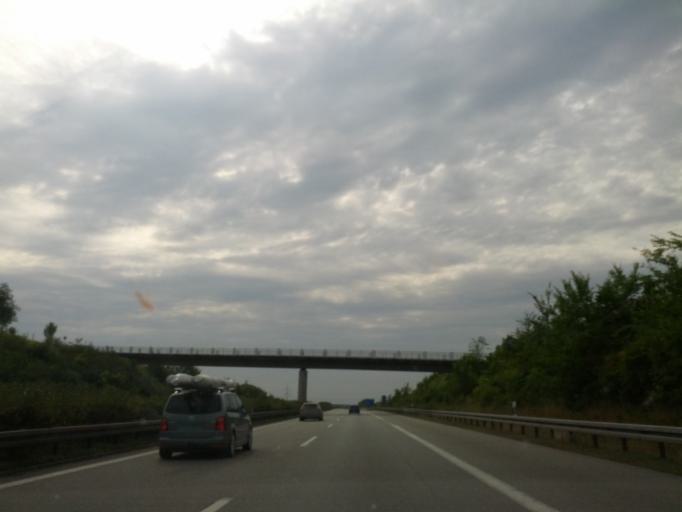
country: DE
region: Mecklenburg-Vorpommern
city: Papendorf
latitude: 54.0215
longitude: 12.1158
